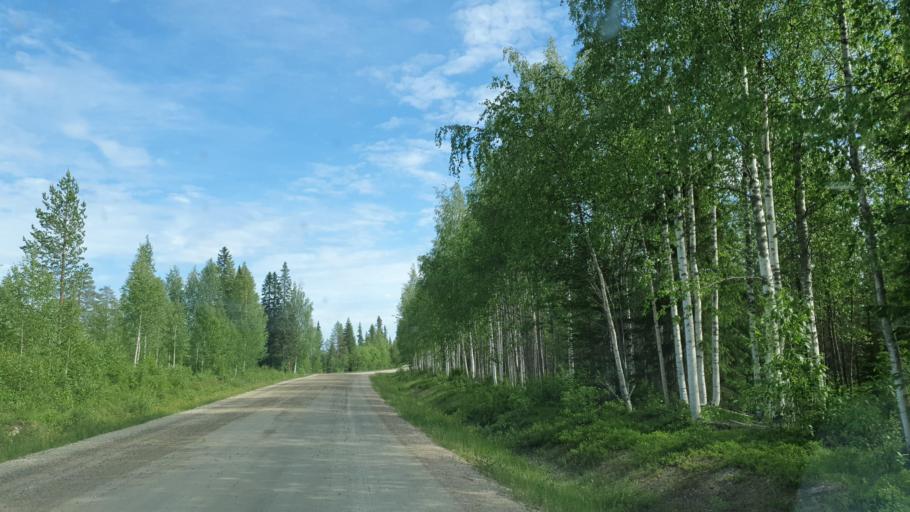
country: FI
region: Kainuu
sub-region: Kehys-Kainuu
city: Kuhmo
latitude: 64.4870
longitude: 29.5190
